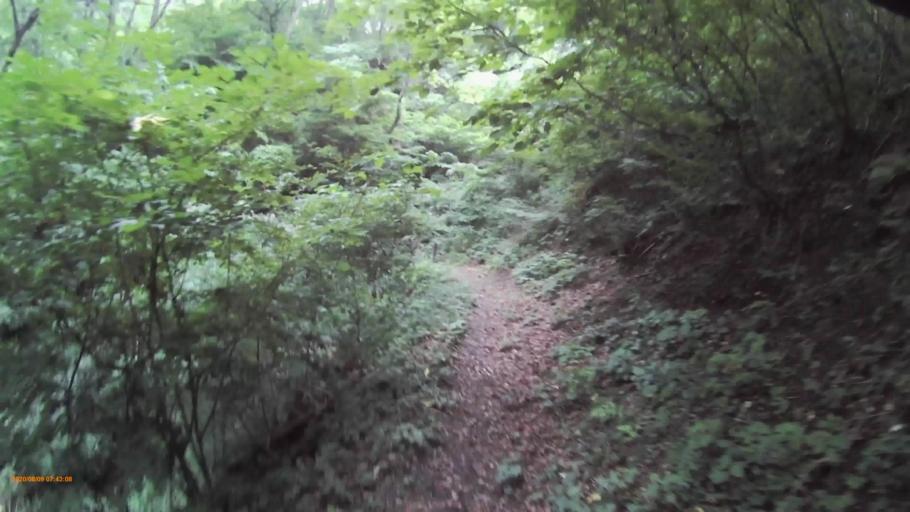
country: JP
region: Nagano
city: Tatsuno
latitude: 35.9572
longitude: 137.8033
